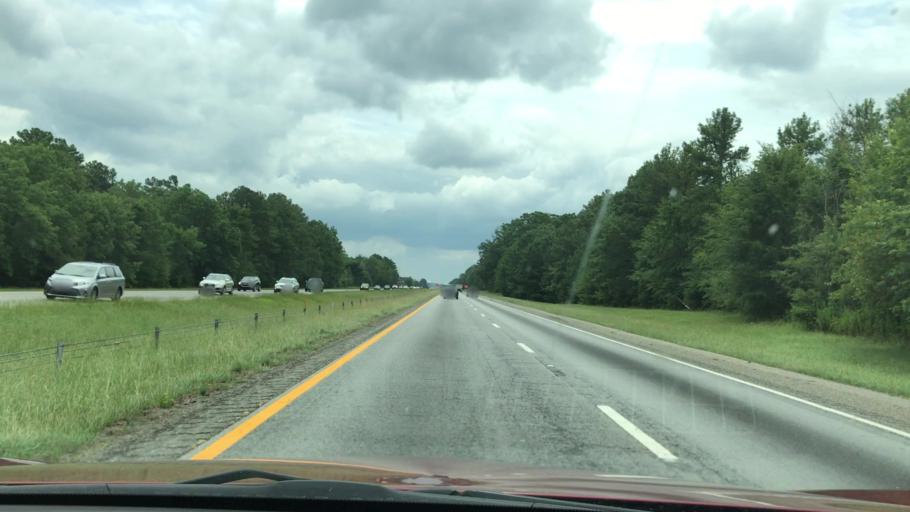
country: US
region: South Carolina
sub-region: Lexington County
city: Irmo
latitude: 34.1208
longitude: -81.1975
